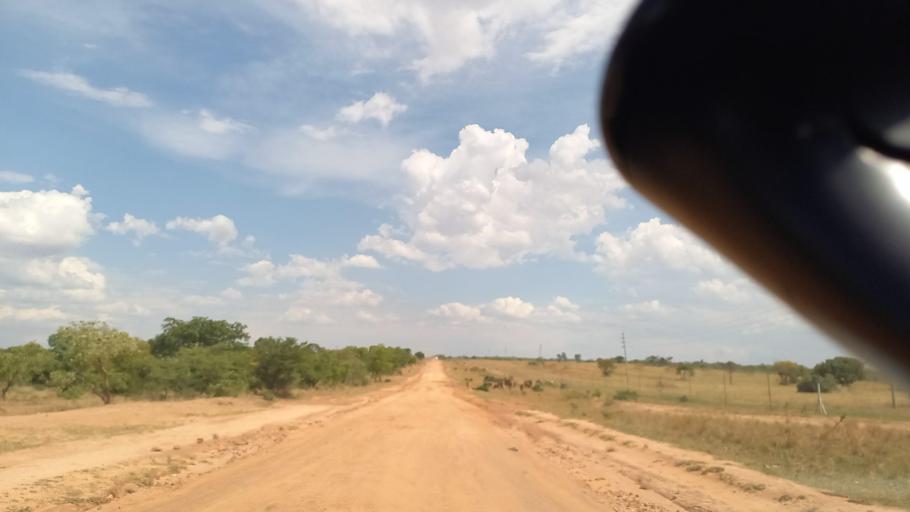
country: ZM
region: Southern
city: Nakambala
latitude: -16.1092
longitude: 28.0256
